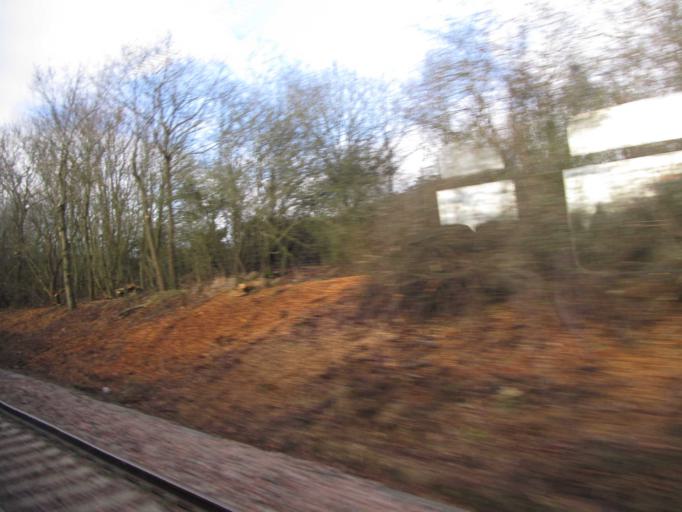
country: GB
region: England
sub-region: Hampshire
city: Old Basing
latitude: 51.2995
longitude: -1.0572
